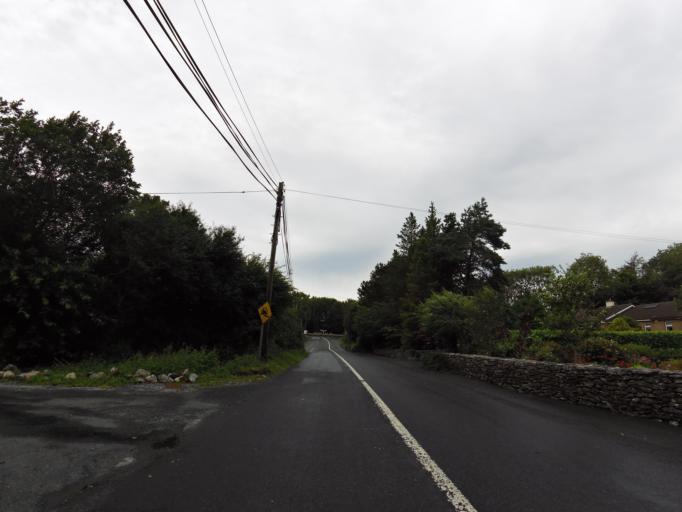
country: IE
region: Connaught
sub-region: County Galway
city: Gaillimh
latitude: 53.3016
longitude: -9.0663
